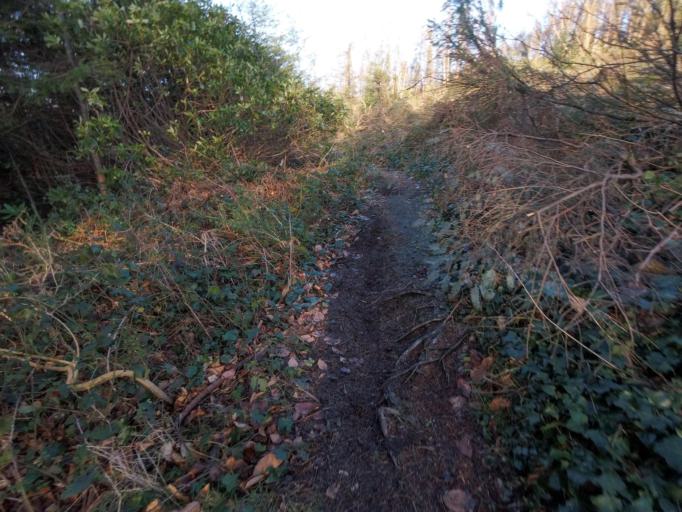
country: IE
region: Munster
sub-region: Waterford
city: Waterford
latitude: 52.2665
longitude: -7.0167
